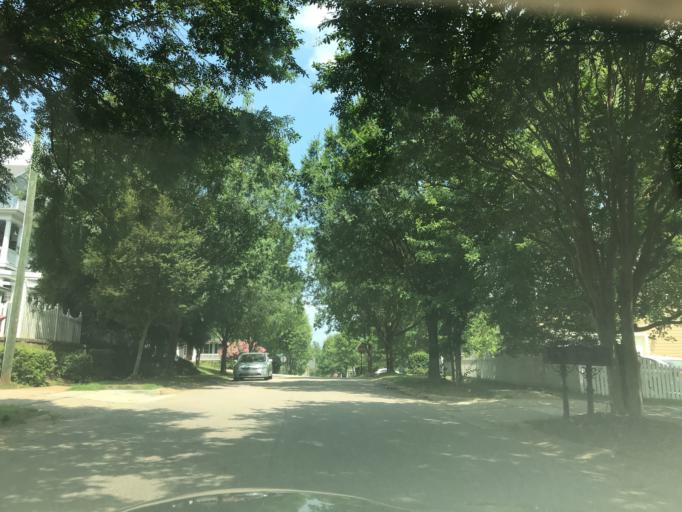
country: US
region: North Carolina
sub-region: Wake County
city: Wake Forest
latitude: 35.9292
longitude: -78.5692
